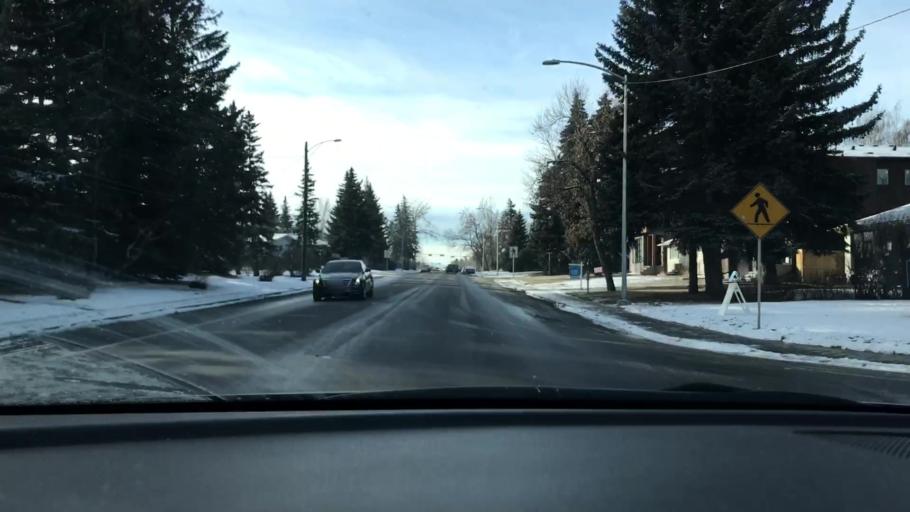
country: CA
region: Alberta
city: Calgary
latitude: 51.0238
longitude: -114.1369
